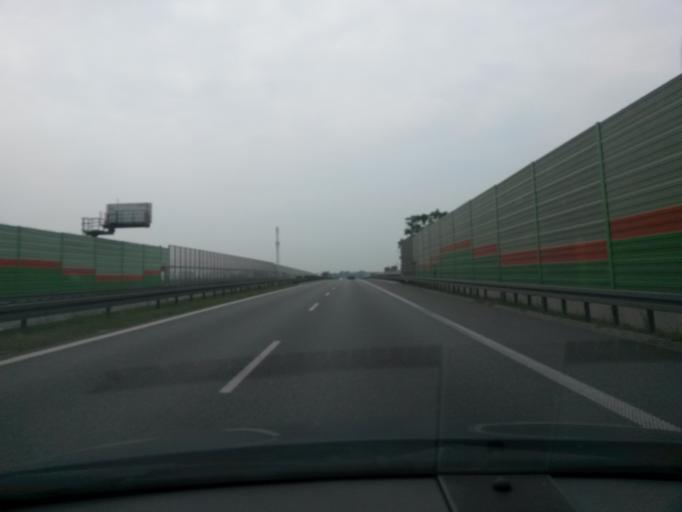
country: PL
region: Lodz Voivodeship
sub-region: Piotrkow Trybunalski
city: Piotrkow Trybunalski
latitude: 51.4426
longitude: 19.6916
